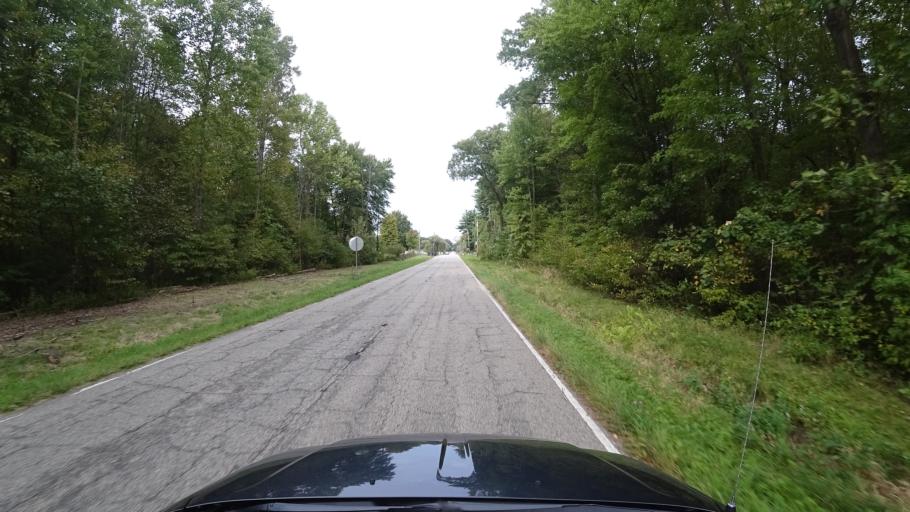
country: US
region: Indiana
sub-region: LaPorte County
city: Long Beach
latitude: 41.7181
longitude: -86.8162
